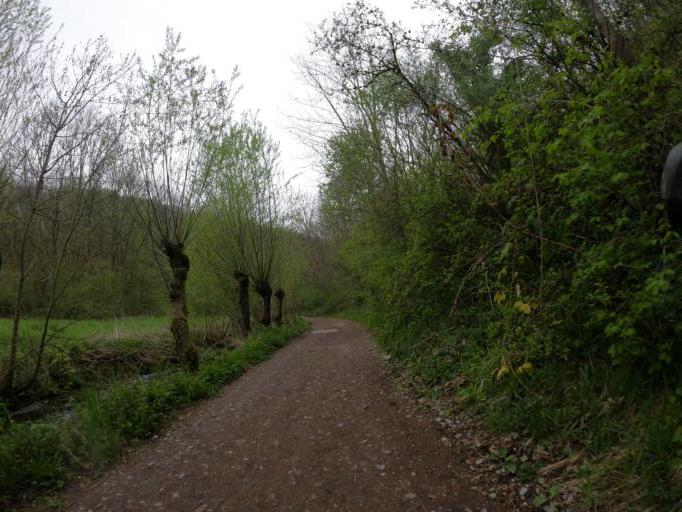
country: DE
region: Baden-Wuerttemberg
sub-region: Regierungsbezirk Stuttgart
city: Markgroningen
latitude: 48.9181
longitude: 9.0818
